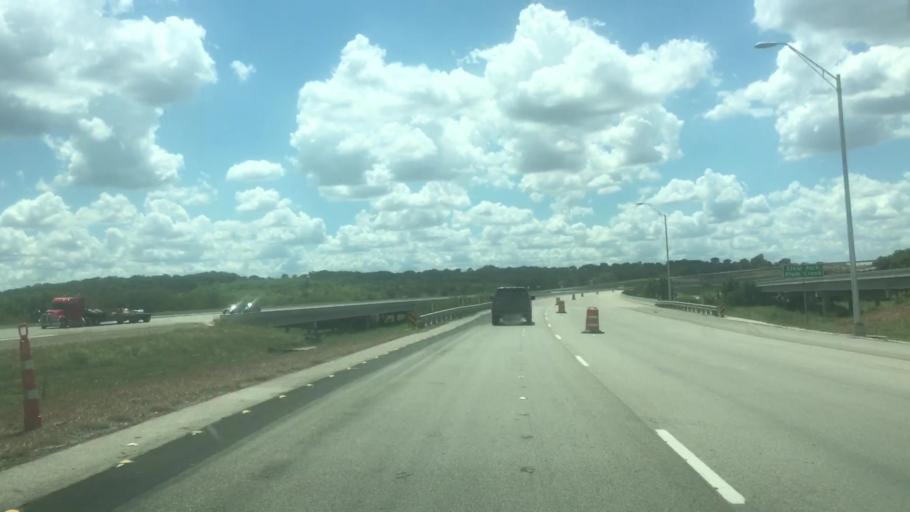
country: US
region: Texas
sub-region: Caldwell County
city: Lockhart
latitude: 29.8614
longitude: -97.7086
